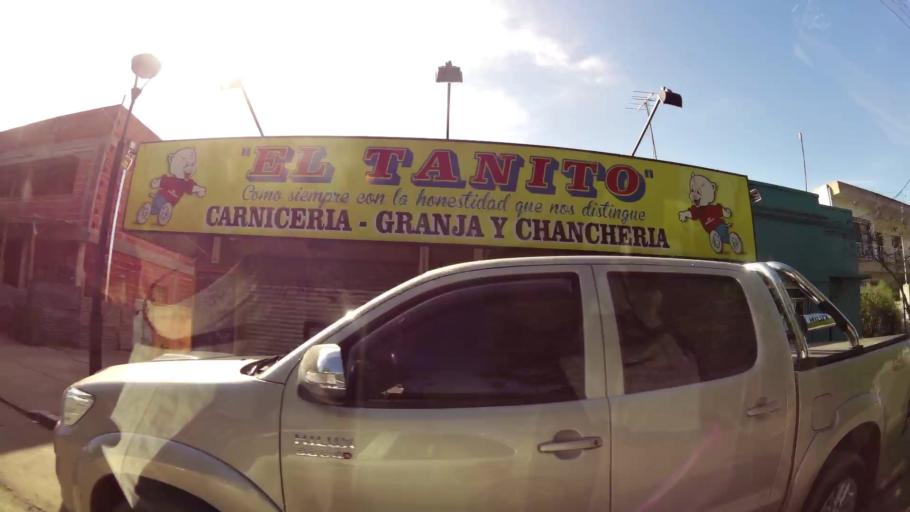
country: AR
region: Buenos Aires
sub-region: Partido de Quilmes
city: Quilmes
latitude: -34.8023
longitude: -58.2206
